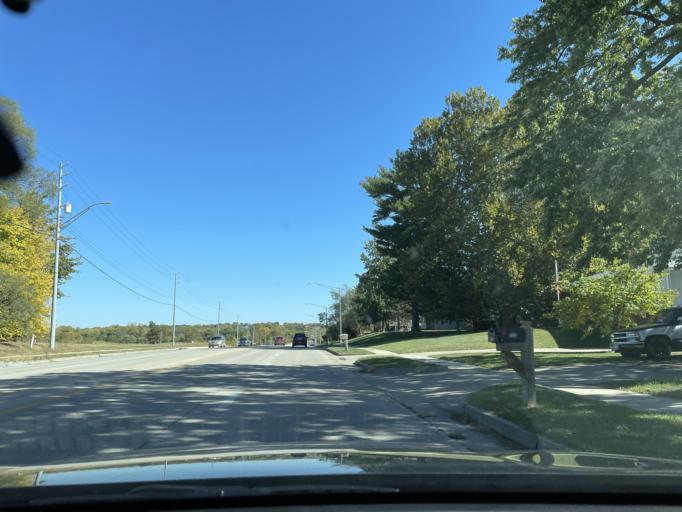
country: US
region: Missouri
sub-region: Andrew County
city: Country Club Village
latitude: 39.7813
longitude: -94.7717
